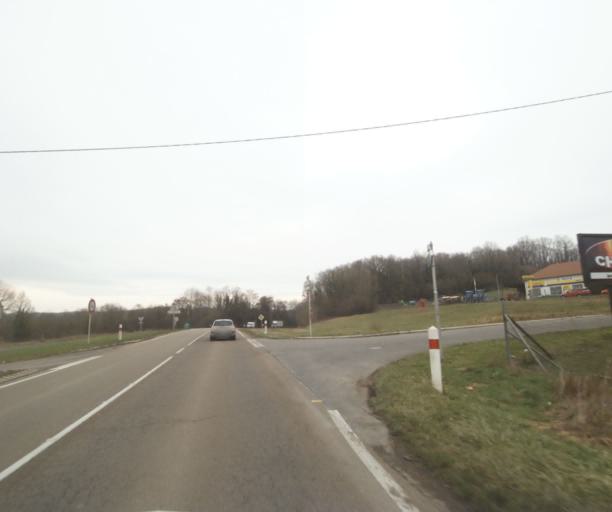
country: FR
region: Champagne-Ardenne
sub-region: Departement de la Haute-Marne
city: Bienville
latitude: 48.6026
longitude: 5.0318
